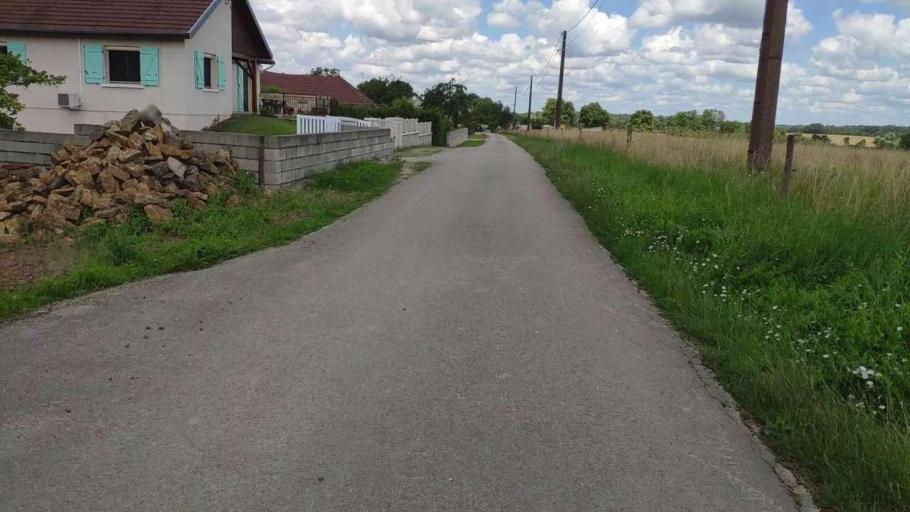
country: FR
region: Franche-Comte
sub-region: Departement du Jura
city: Bletterans
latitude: 46.8377
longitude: 5.4895
